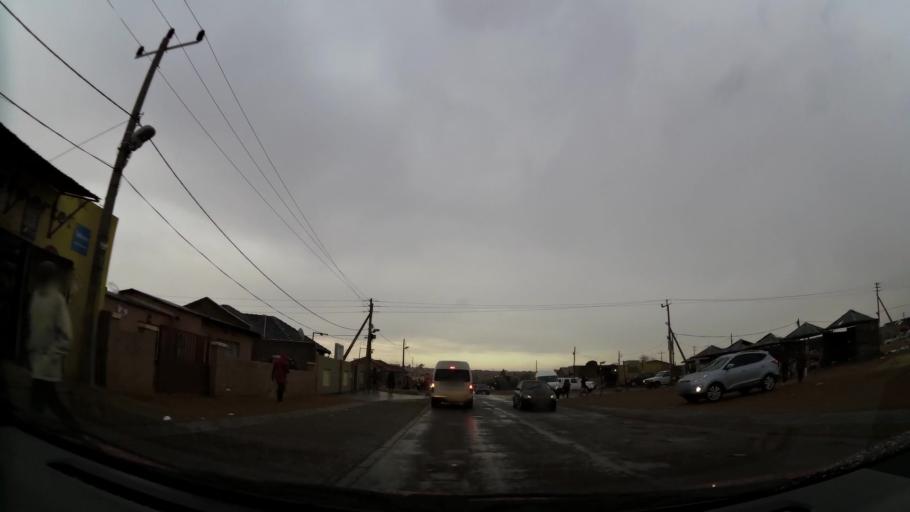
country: ZA
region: Gauteng
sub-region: City of Johannesburg Metropolitan Municipality
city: Roodepoort
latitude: -26.1748
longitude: 27.7914
